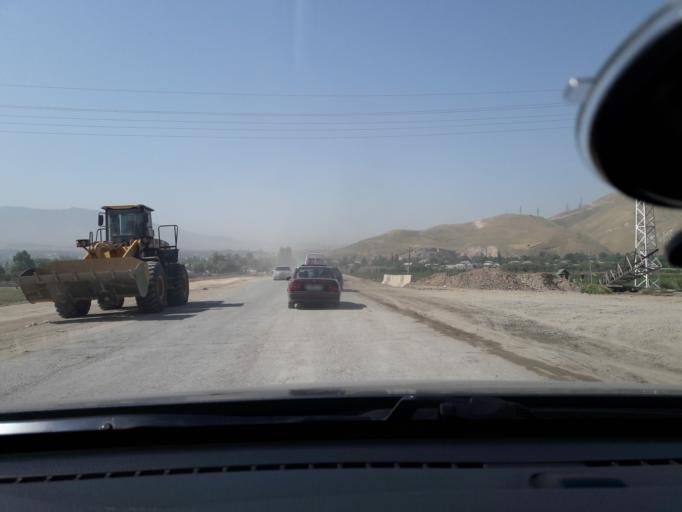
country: TJ
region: Dushanbe
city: Boshkengash
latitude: 38.4528
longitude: 68.7351
